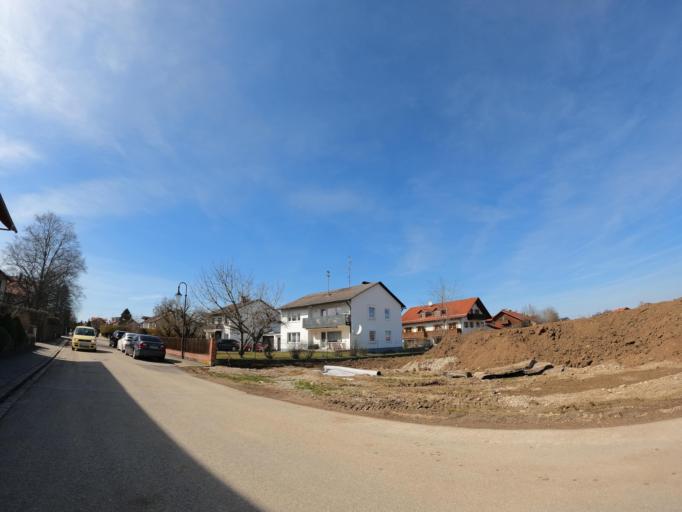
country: DE
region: Bavaria
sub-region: Upper Bavaria
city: Brunnthal
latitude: 48.0060
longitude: 11.6885
